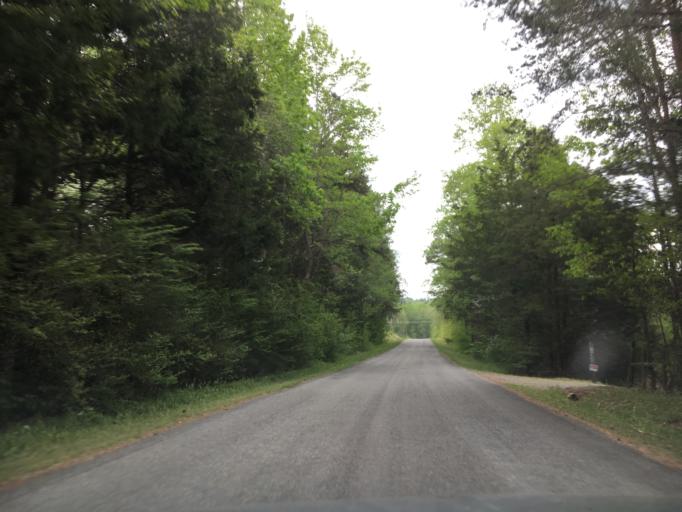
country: US
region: Virginia
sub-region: Halifax County
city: Halifax
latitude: 36.7995
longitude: -78.9322
